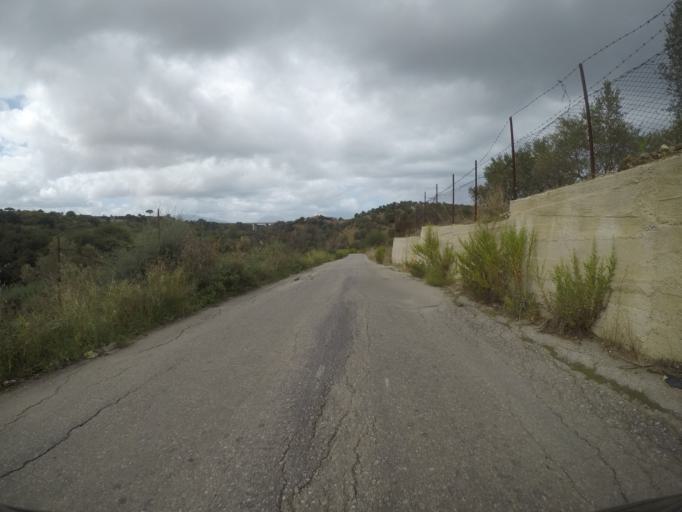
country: IT
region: Sicily
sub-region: Palermo
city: Partinico
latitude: 38.0824
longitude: 13.1082
